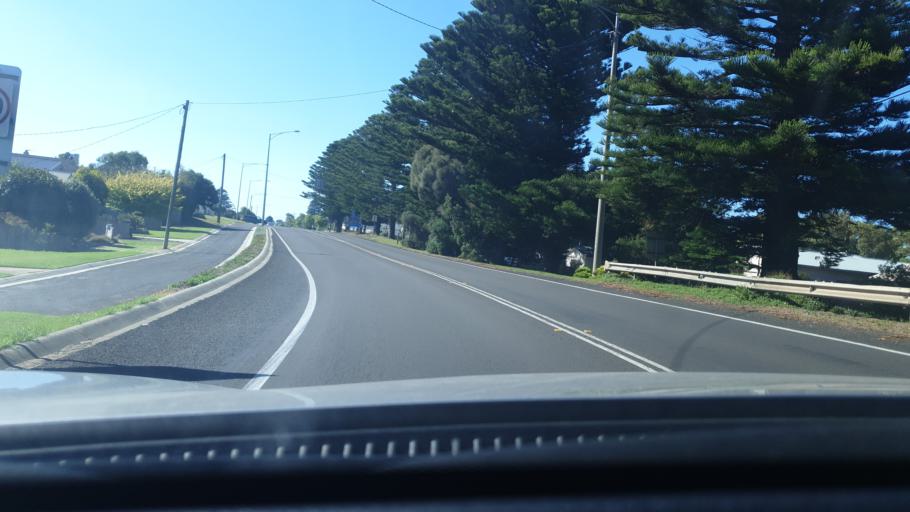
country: AU
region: Victoria
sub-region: Moyne
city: Port Fairy
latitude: -38.3842
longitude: 142.2288
